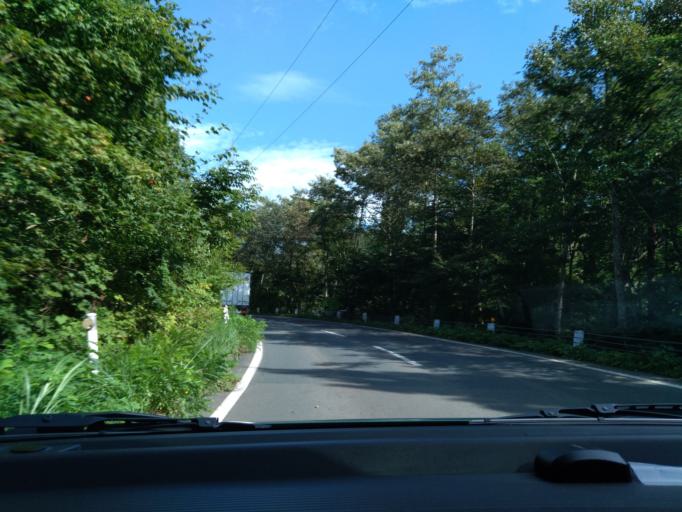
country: JP
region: Iwate
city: Shizukuishi
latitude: 39.6377
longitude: 141.0175
